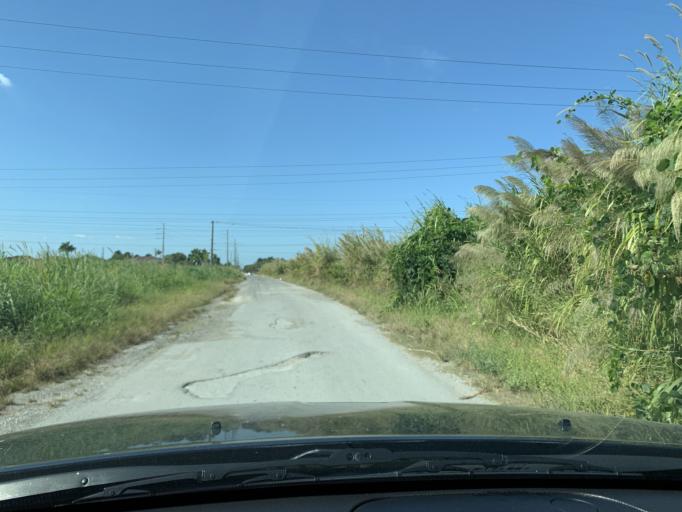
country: US
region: Florida
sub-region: Miami-Dade County
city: Three Lakes
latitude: 25.6414
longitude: -80.3965
